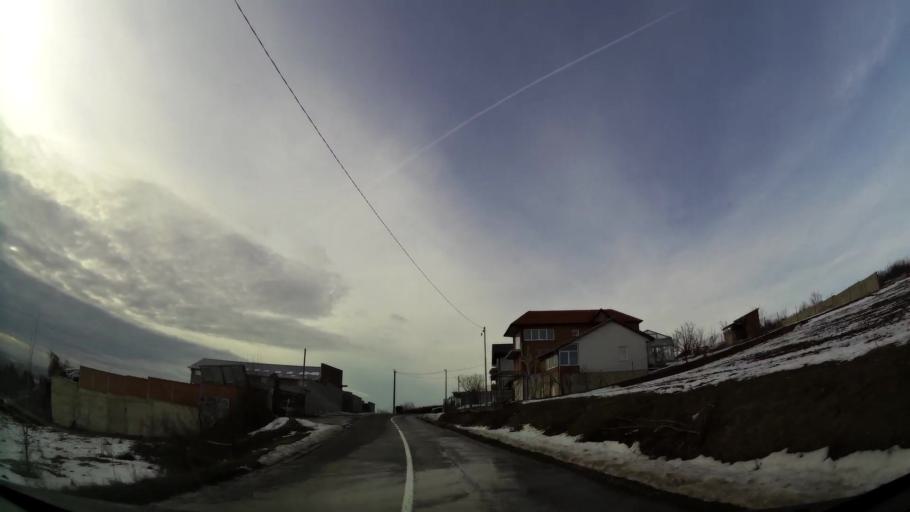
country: RS
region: Central Serbia
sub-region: Belgrade
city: Zvezdara
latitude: 44.7261
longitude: 20.5072
